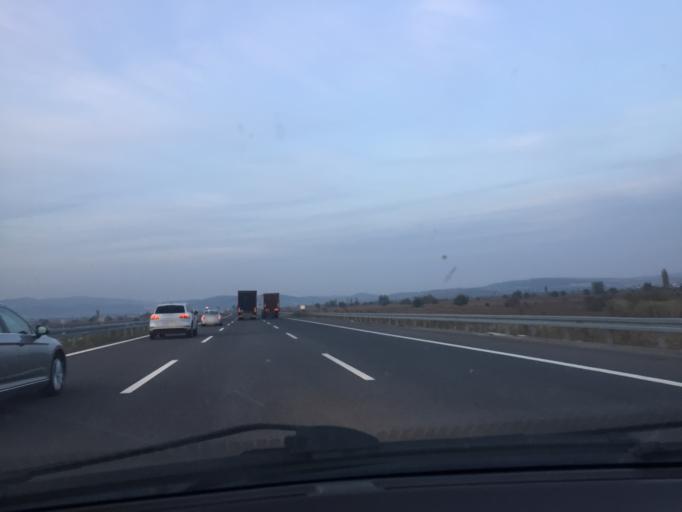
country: TR
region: Manisa
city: Halitpasa
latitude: 38.7461
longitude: 27.6594
